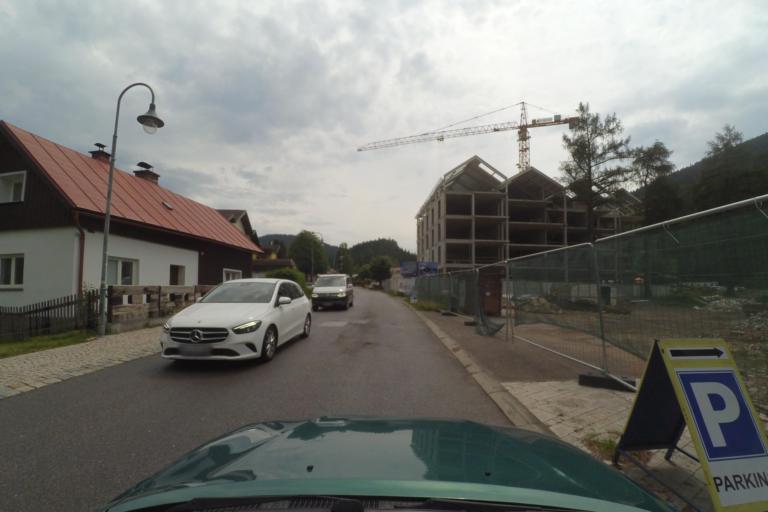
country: CZ
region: Liberecky
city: Harrachov
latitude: 50.7710
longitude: 15.4322
